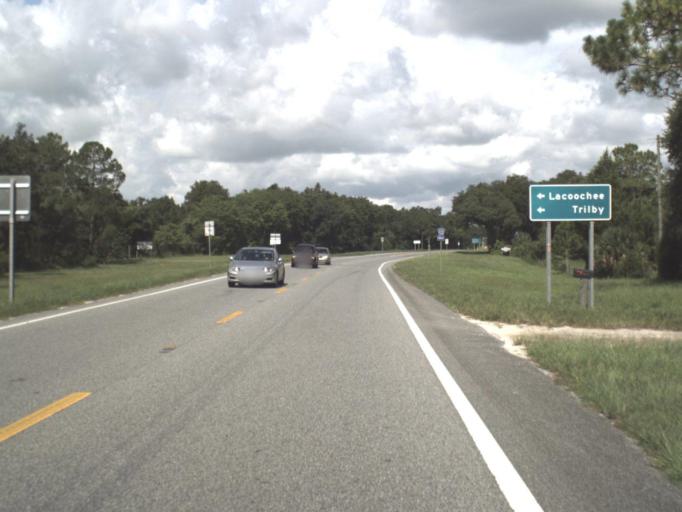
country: US
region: Florida
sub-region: Hernando County
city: Ridge Manor
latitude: 28.5072
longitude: -82.1528
